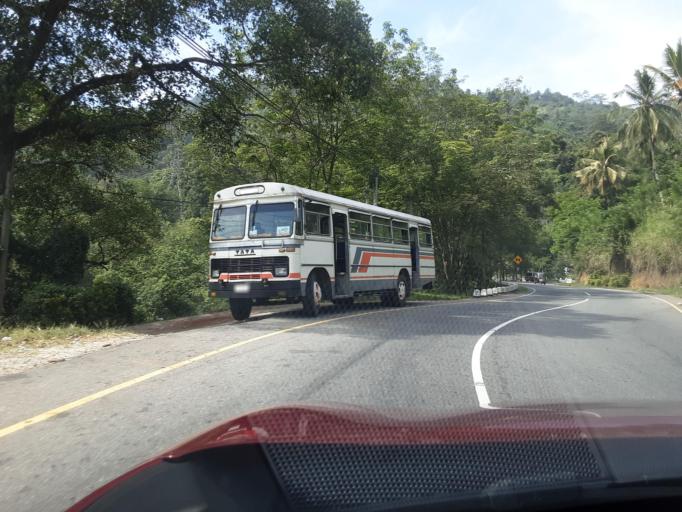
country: LK
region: Uva
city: Badulla
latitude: 6.9670
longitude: 81.0903
